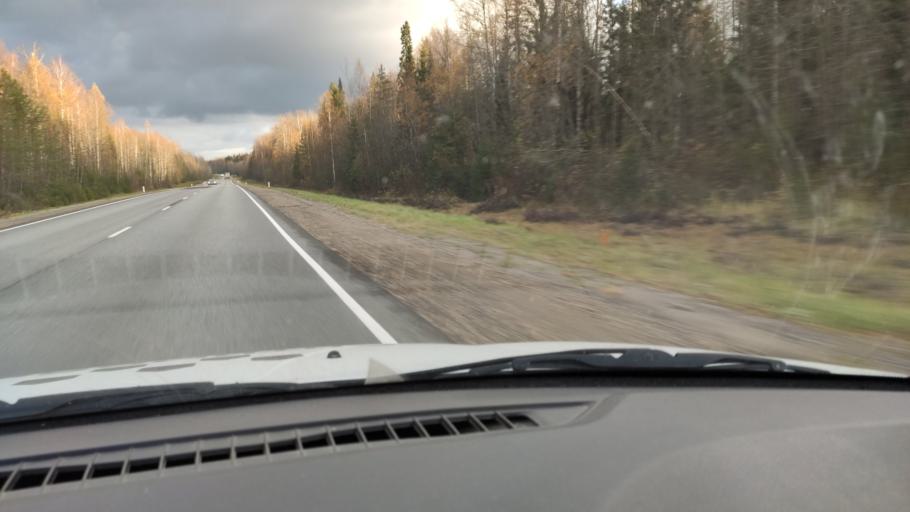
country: RU
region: Kirov
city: Chernaya Kholunitsa
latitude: 58.7820
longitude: 51.9106
